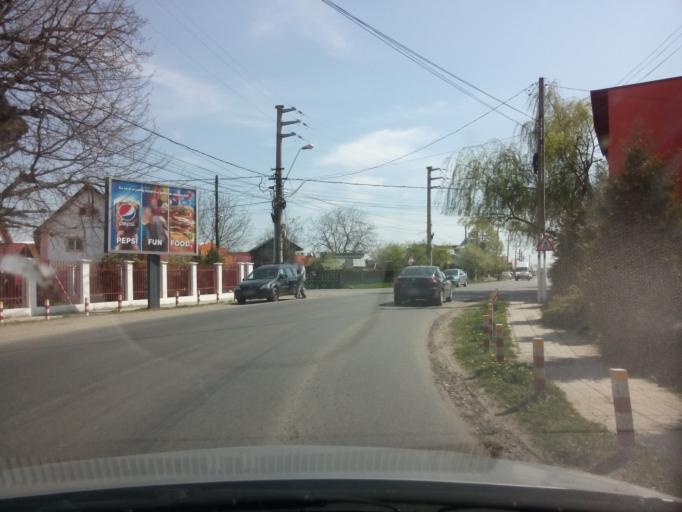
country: RO
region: Ilfov
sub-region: Comuna Corbeanca
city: Corbeanca
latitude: 44.6015
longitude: 26.0660
